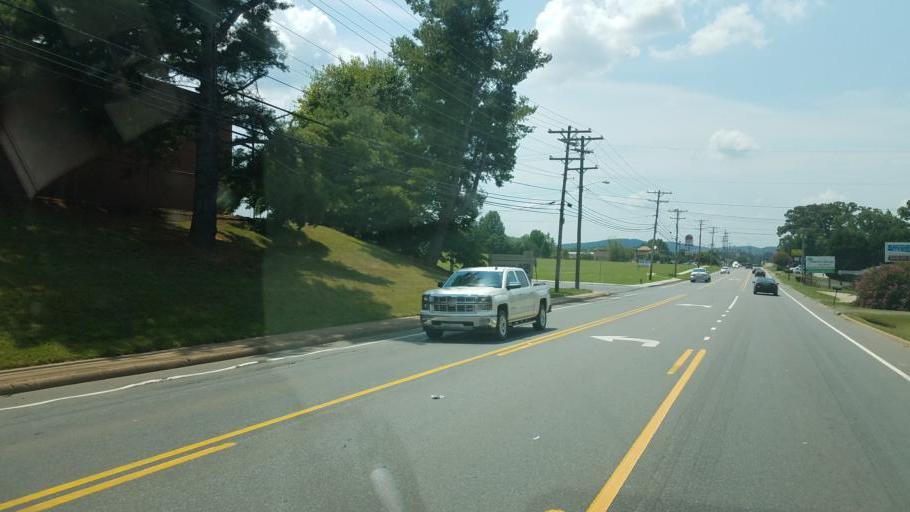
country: US
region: North Carolina
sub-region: Cleveland County
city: Kings Mountain
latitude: 35.2339
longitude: -81.3332
